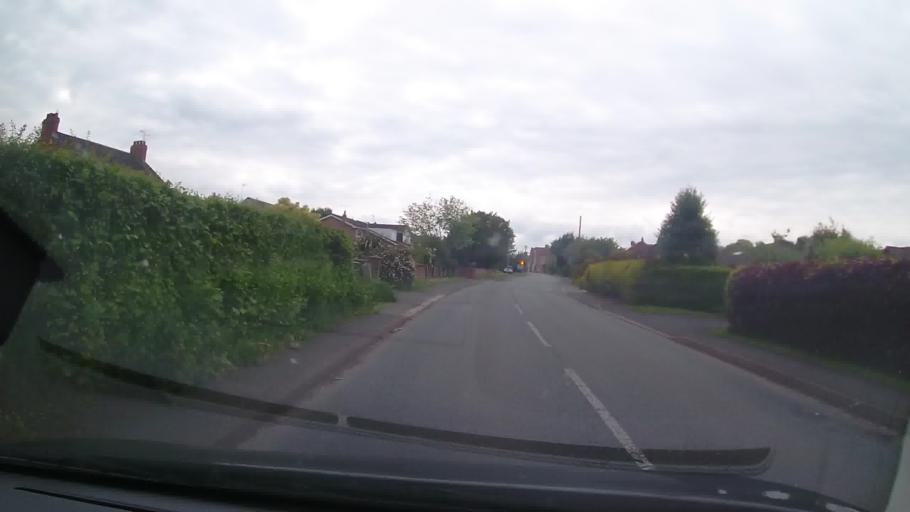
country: GB
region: Wales
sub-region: Wrexham
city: Overton
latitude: 52.9688
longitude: -2.9308
